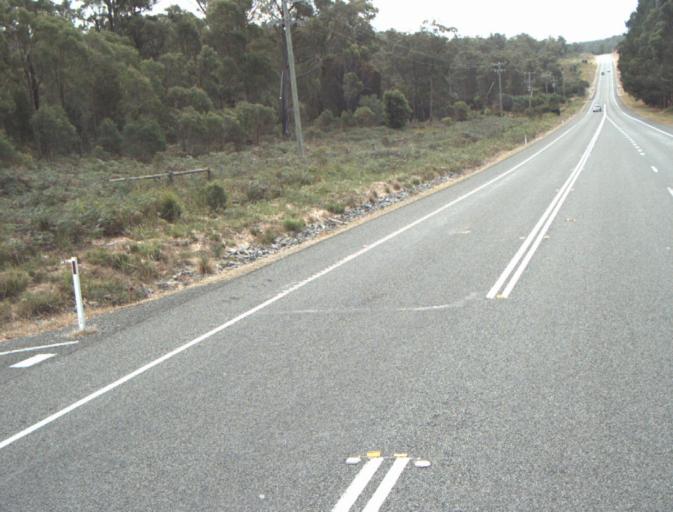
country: AU
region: Tasmania
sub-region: Launceston
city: Mayfield
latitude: -41.2758
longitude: 147.0368
